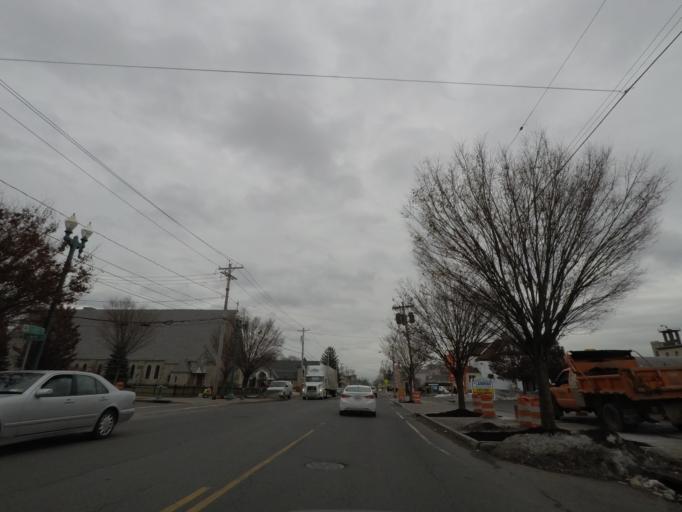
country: US
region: New York
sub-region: Schenectady County
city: Schenectady
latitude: 42.7991
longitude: -73.9253
